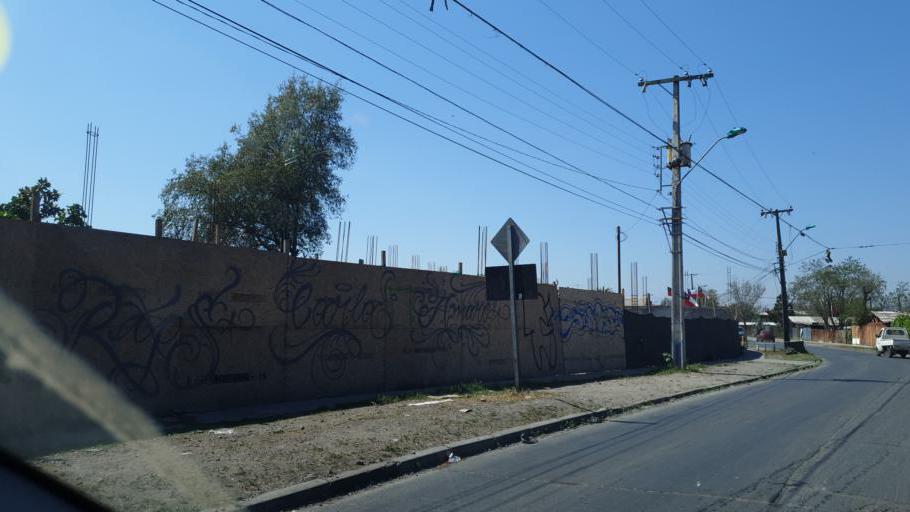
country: CL
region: Santiago Metropolitan
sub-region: Provincia de Talagante
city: Talagante
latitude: -33.6603
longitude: -70.9329
